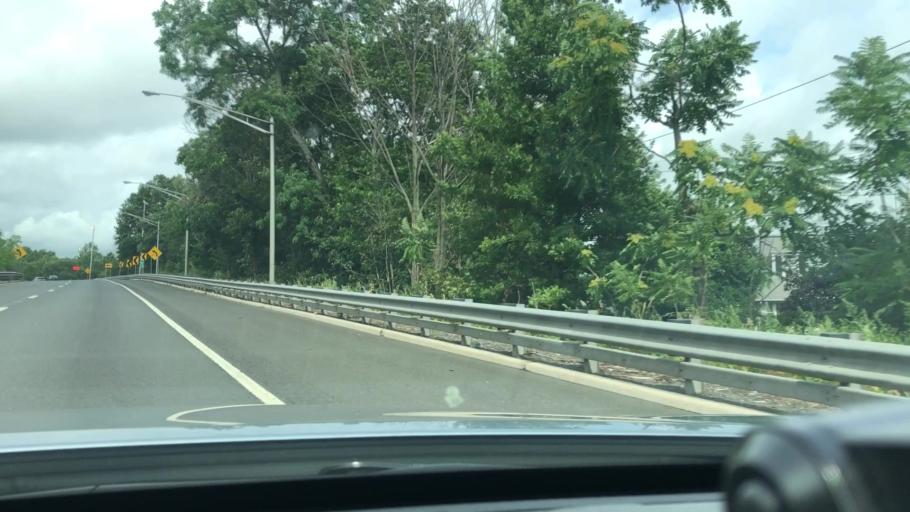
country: US
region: New Jersey
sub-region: Union County
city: Linden
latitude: 40.6415
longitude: -74.2272
